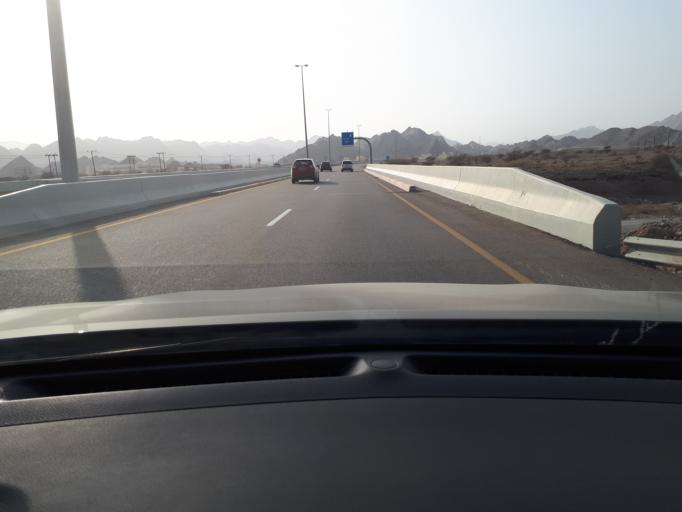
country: OM
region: Muhafazat Masqat
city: Muscat
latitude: 23.3033
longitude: 58.7347
